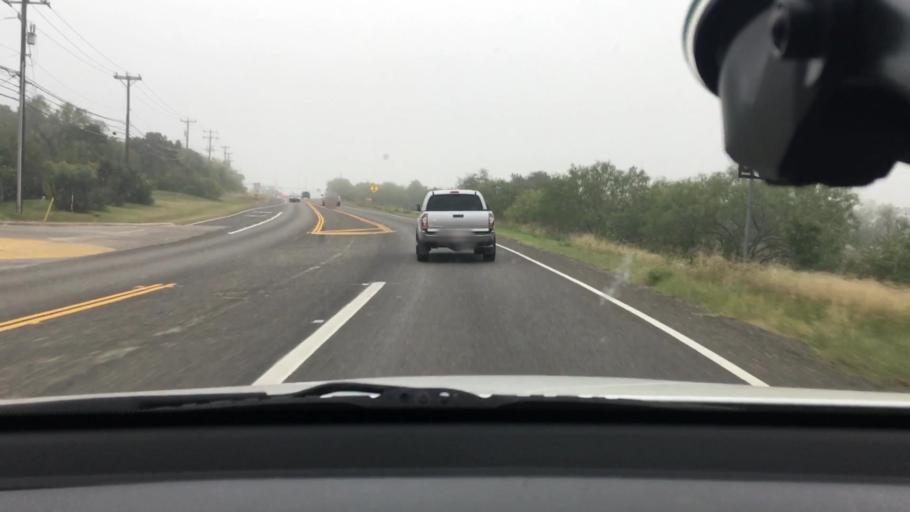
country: US
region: Texas
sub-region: Comal County
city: Garden Ridge
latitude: 29.6210
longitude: -98.2949
